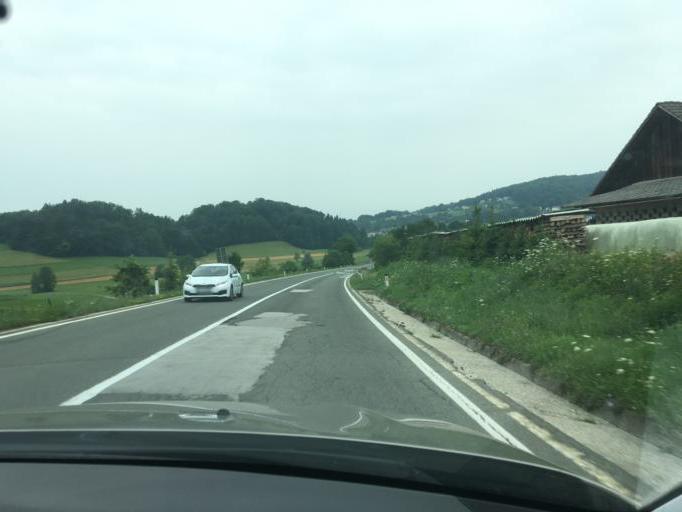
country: SI
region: Grosuplje
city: Smarje-Sap
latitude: 45.9800
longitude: 14.5952
